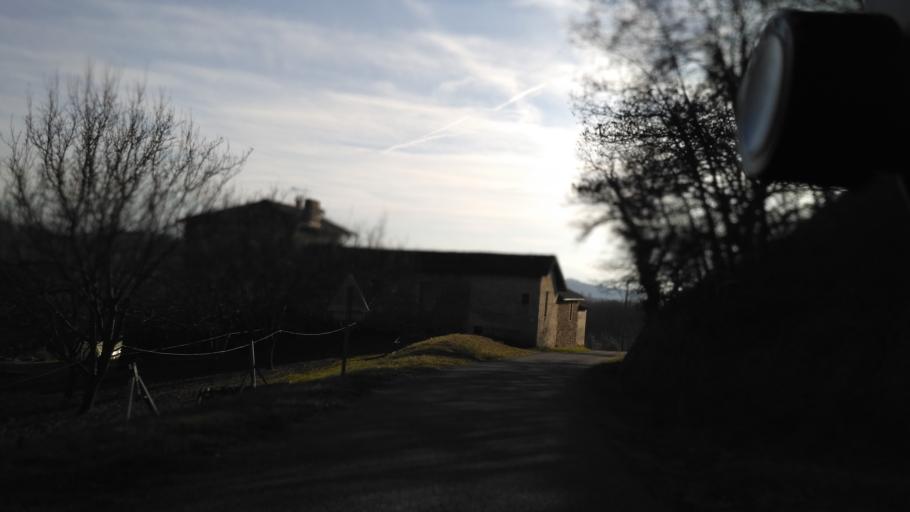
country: FR
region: Rhone-Alpes
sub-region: Departement de l'Isere
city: Saint-Lattier
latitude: 45.1314
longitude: 5.1519
